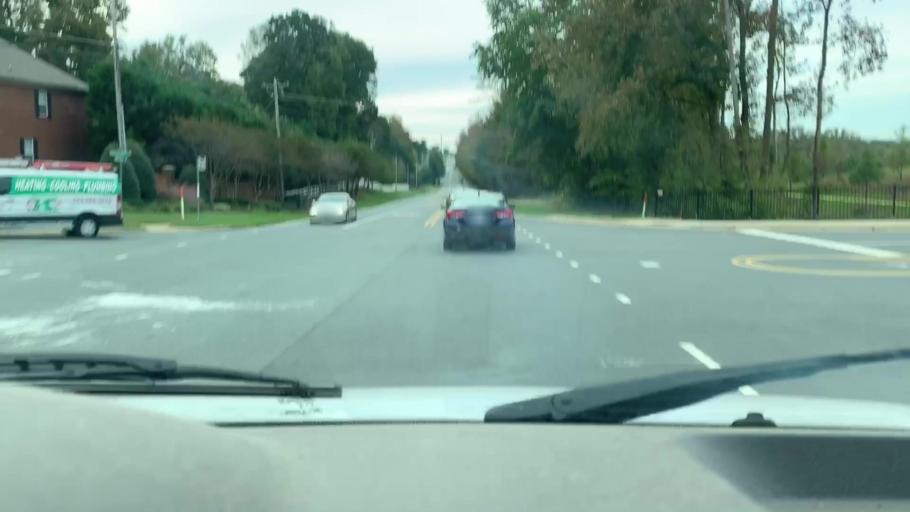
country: US
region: North Carolina
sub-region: Mecklenburg County
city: Huntersville
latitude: 35.4311
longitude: -80.8639
